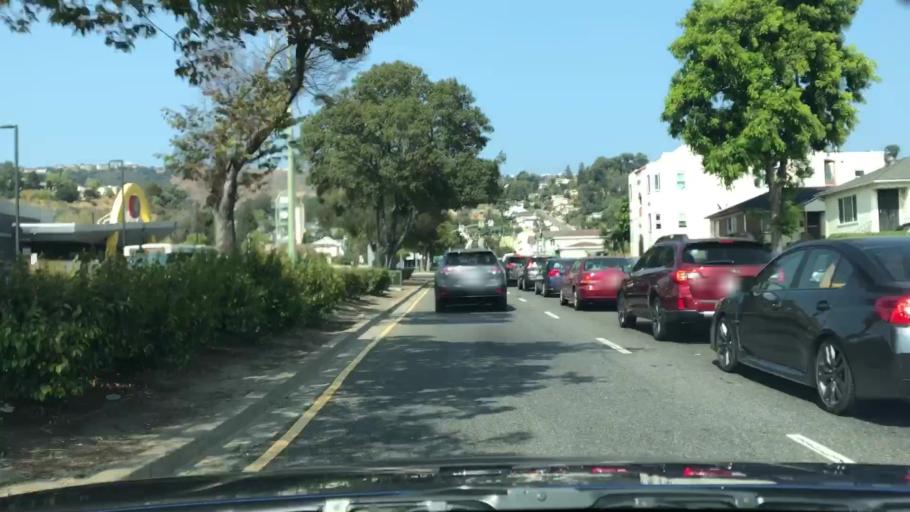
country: US
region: California
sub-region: Alameda County
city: San Leandro
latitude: 37.7675
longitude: -122.1744
